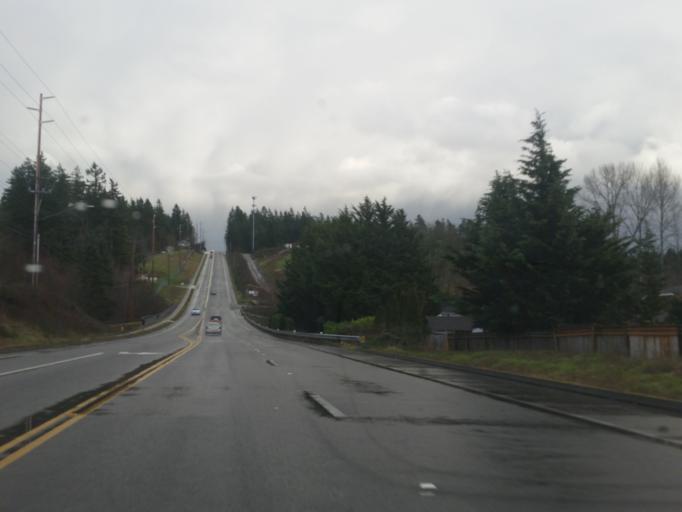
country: US
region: Washington
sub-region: Snohomish County
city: Brier
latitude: 47.7916
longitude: -122.2513
